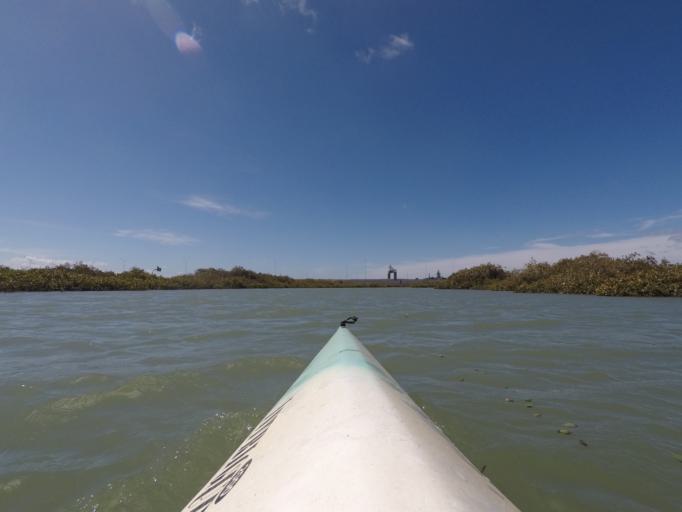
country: NZ
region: Auckland
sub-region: Auckland
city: Rosebank
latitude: -36.8738
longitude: 174.6948
